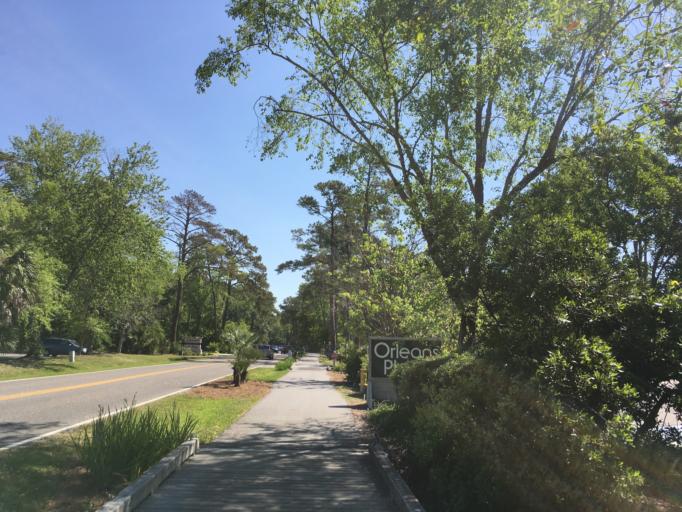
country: US
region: South Carolina
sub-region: Beaufort County
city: Hilton Head Island
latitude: 32.1559
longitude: -80.7578
